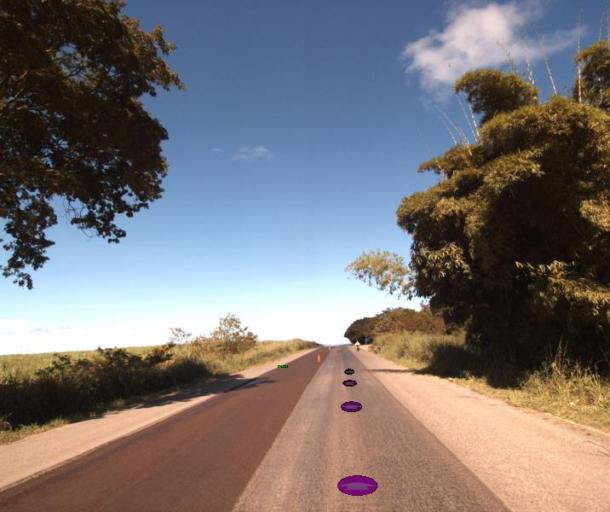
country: BR
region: Goias
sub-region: Itapaci
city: Itapaci
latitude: -15.1074
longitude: -49.4836
